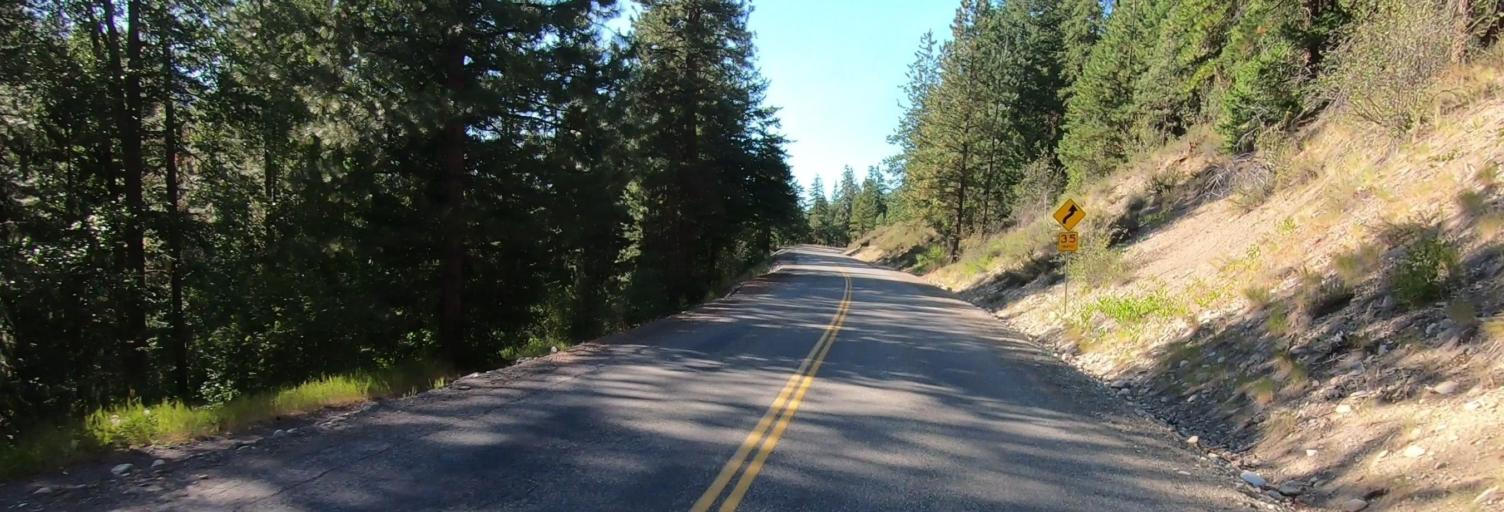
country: US
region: Washington
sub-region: Chelan County
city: Granite Falls
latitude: 48.5695
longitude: -120.3632
